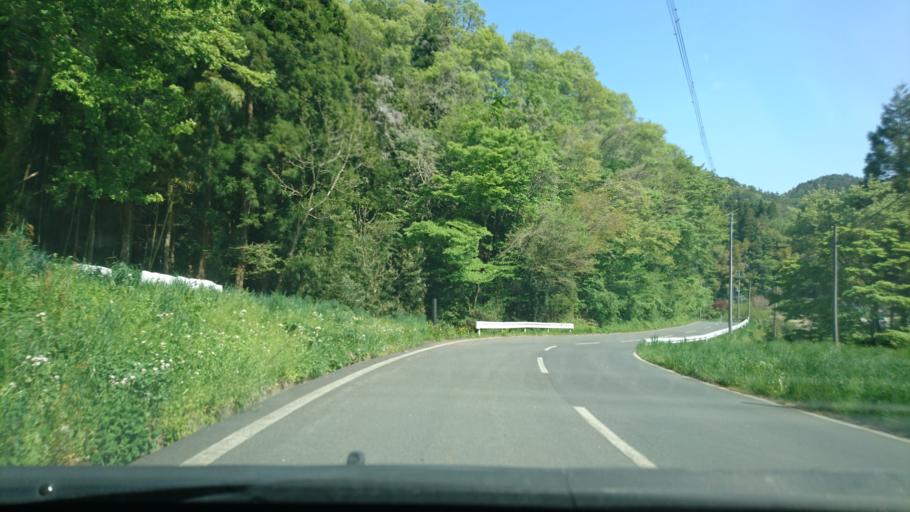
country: JP
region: Iwate
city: Ichinoseki
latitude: 38.9364
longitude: 141.2784
